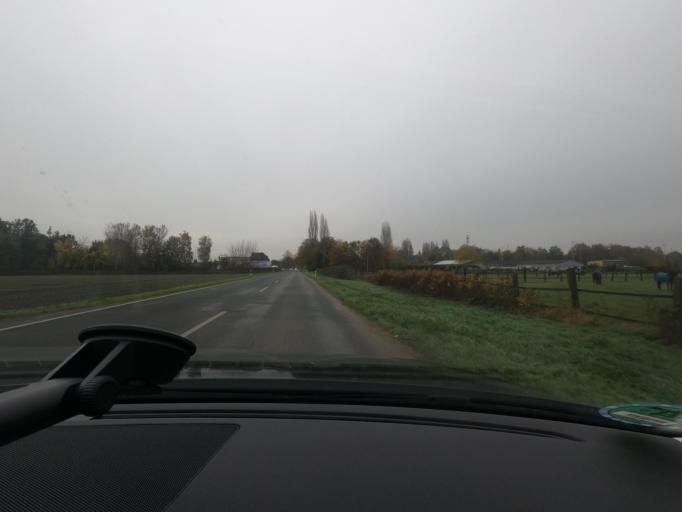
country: DE
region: North Rhine-Westphalia
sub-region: Regierungsbezirk Dusseldorf
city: Wachtendonk
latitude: 51.4528
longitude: 6.3599
